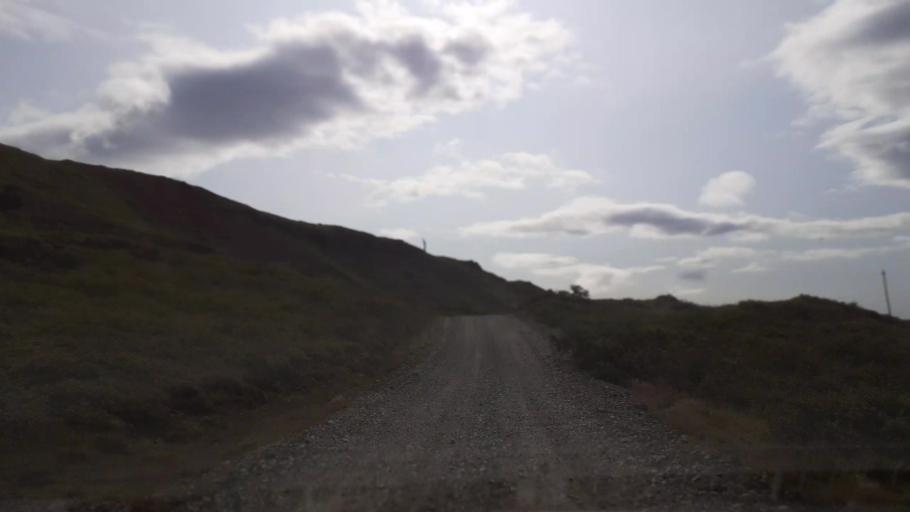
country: IS
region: East
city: Hoefn
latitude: 64.4307
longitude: -14.8882
